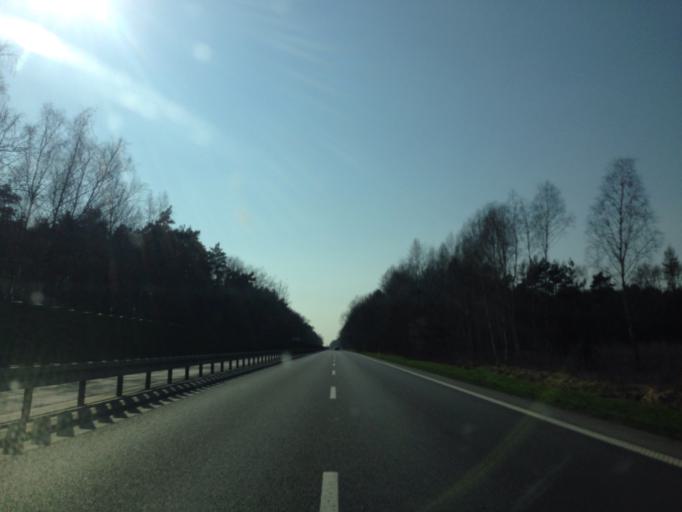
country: PL
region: Lower Silesian Voivodeship
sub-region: Powiat wroclawski
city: Dlugoleka
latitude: 51.1937
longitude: 17.2714
